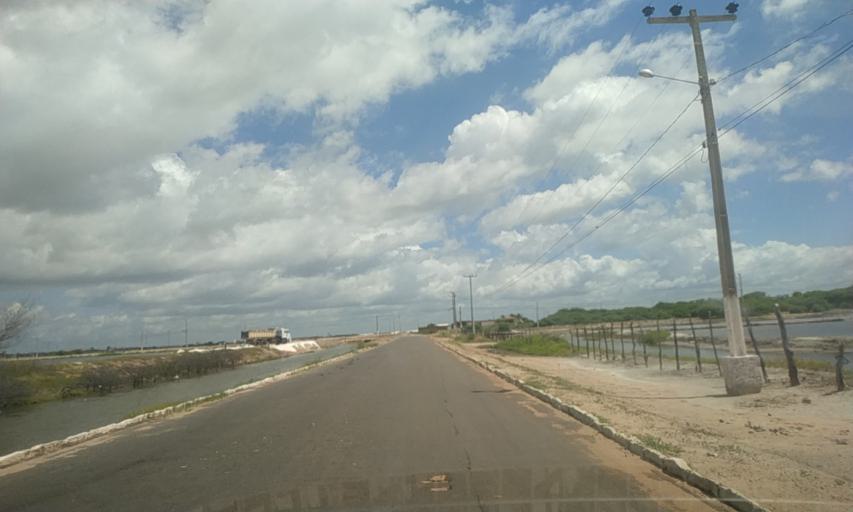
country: BR
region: Rio Grande do Norte
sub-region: Areia Branca
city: Areia Branca
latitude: -4.9346
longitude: -37.1122
